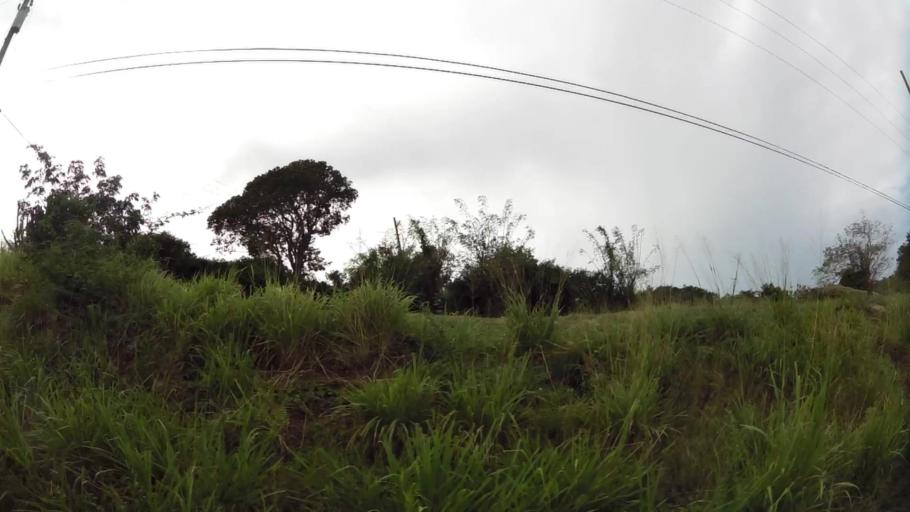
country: AG
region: Saint George
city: Piggotts
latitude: 17.1041
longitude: -61.8124
